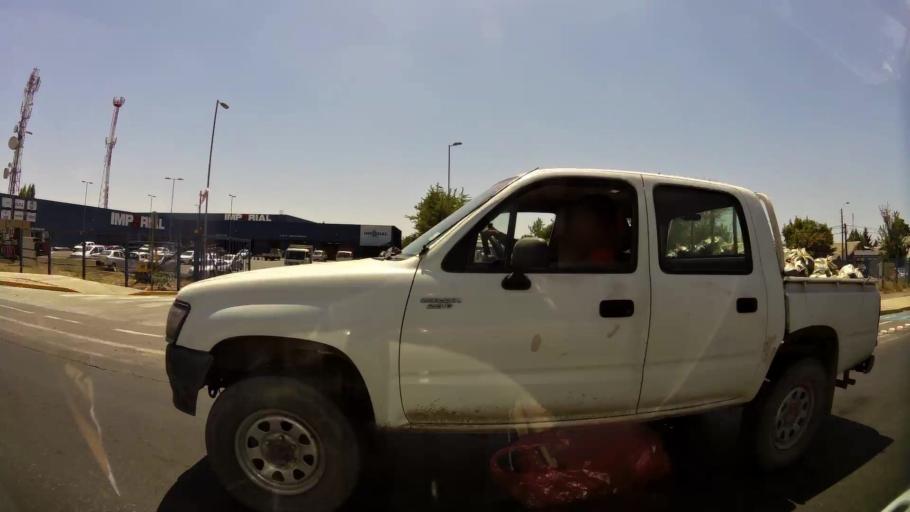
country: CL
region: Maule
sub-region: Provincia de Talca
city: Talca
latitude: -35.4325
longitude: -71.6351
